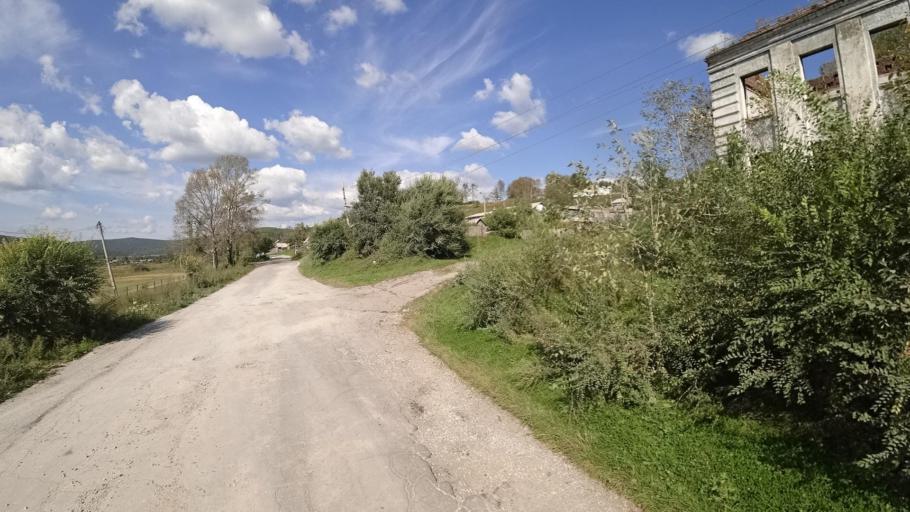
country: RU
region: Jewish Autonomous Oblast
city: Londoko
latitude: 49.0063
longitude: 131.8794
